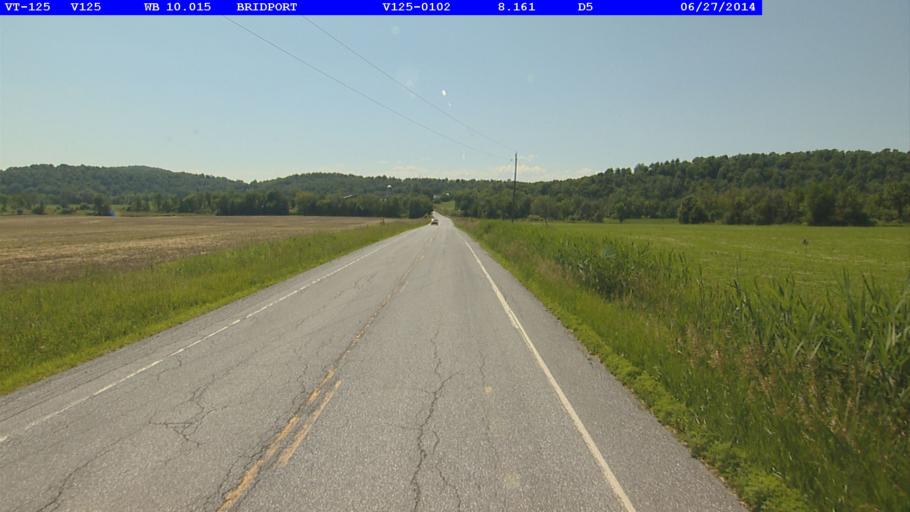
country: US
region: Vermont
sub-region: Addison County
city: Middlebury (village)
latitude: 43.9966
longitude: -73.2578
